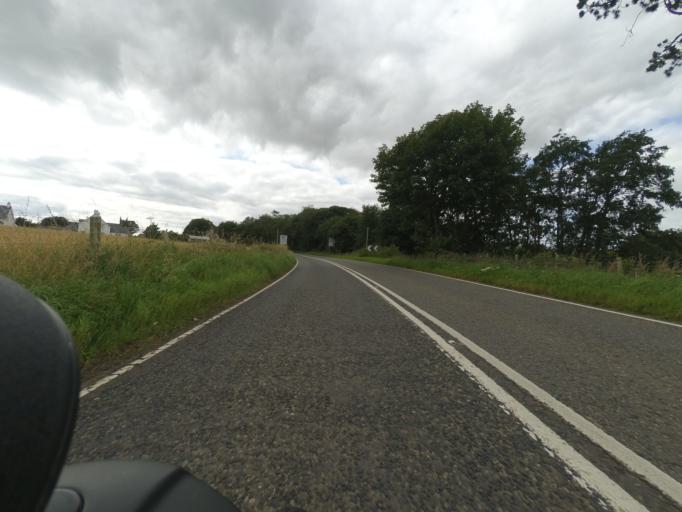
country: GB
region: Scotland
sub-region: Aberdeenshire
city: Laurencekirk
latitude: 56.7770
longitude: -2.4133
